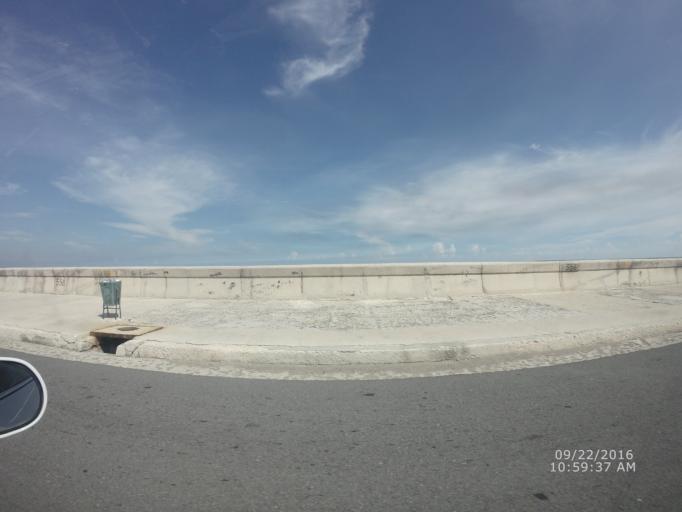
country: CU
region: La Habana
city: Havana
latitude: 23.1465
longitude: -82.3906
